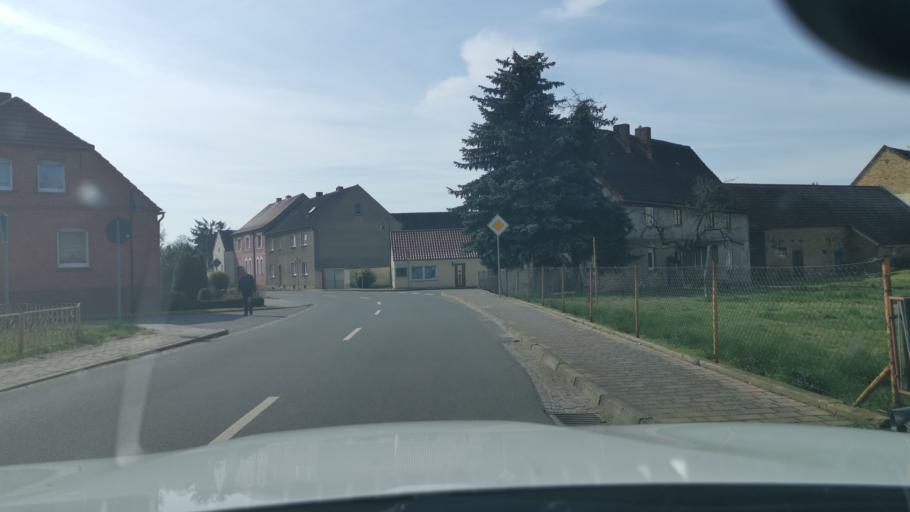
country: DE
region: Saxony-Anhalt
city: Zahna
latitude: 51.8895
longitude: 12.8195
